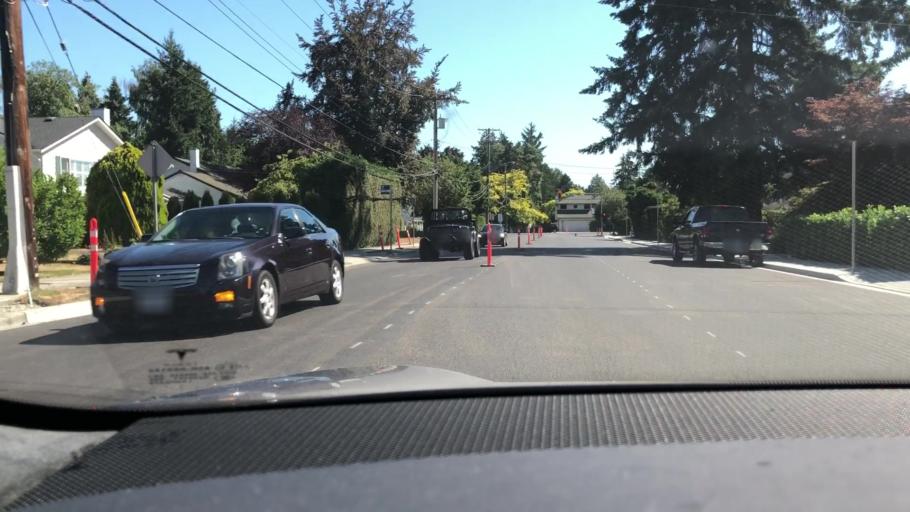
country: US
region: Washington
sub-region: Whatcom County
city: Point Roberts
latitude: 49.0259
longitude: -123.0798
